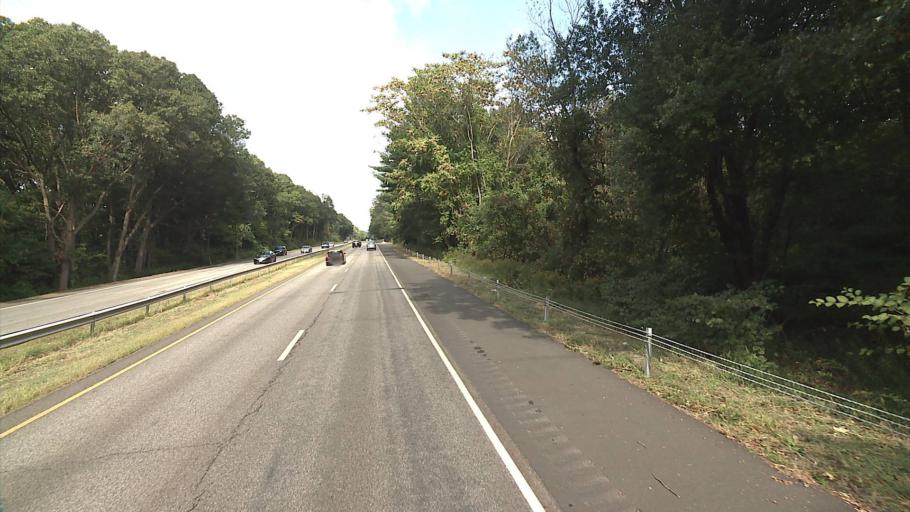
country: US
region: Connecticut
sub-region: New Haven County
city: Wallingford
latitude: 41.4706
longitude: -72.8283
